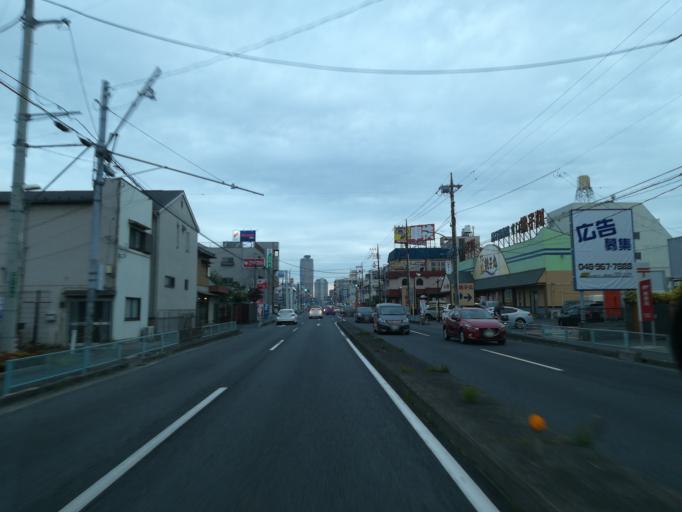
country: JP
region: Saitama
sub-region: Kawaguchi-shi
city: Hatogaya-honcho
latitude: 35.8134
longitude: 139.7354
